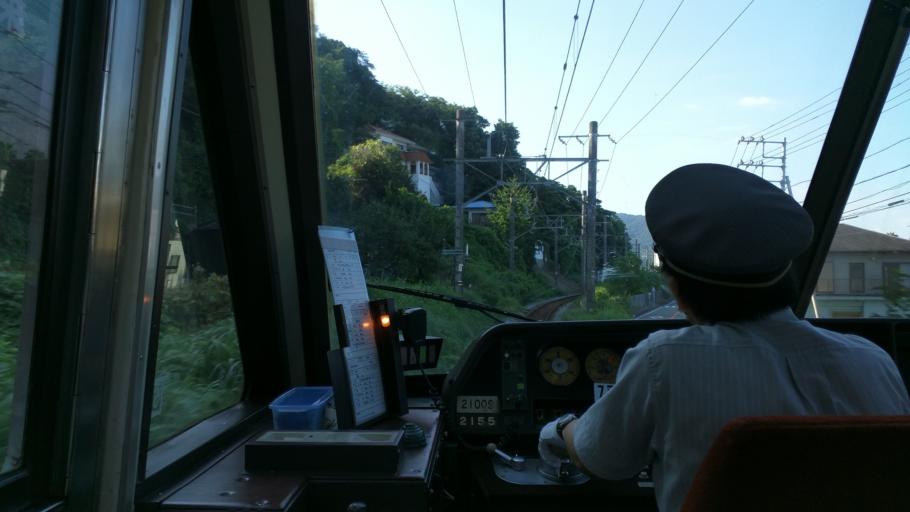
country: JP
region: Shizuoka
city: Ito
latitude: 34.9854
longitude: 139.0926
